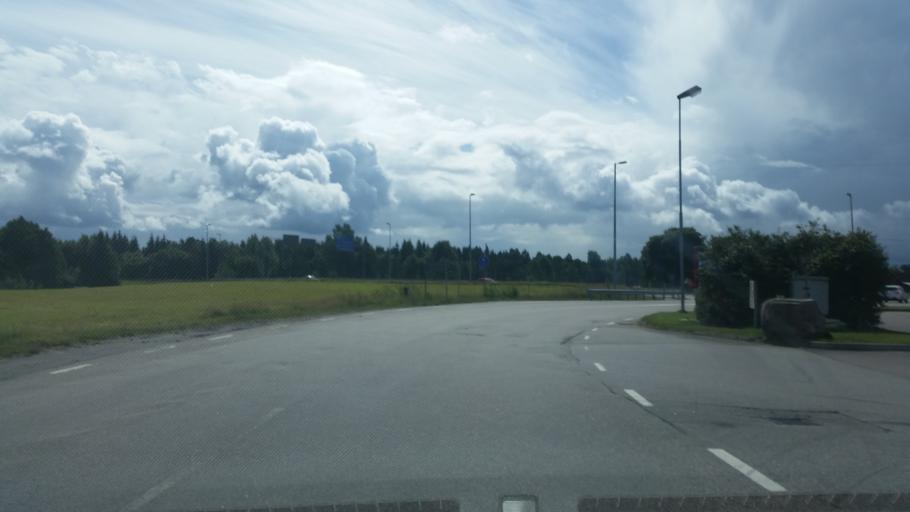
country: SE
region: Vaestra Goetaland
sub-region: Ulricehamns Kommun
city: Ulricehamn
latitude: 57.7798
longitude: 13.6626
